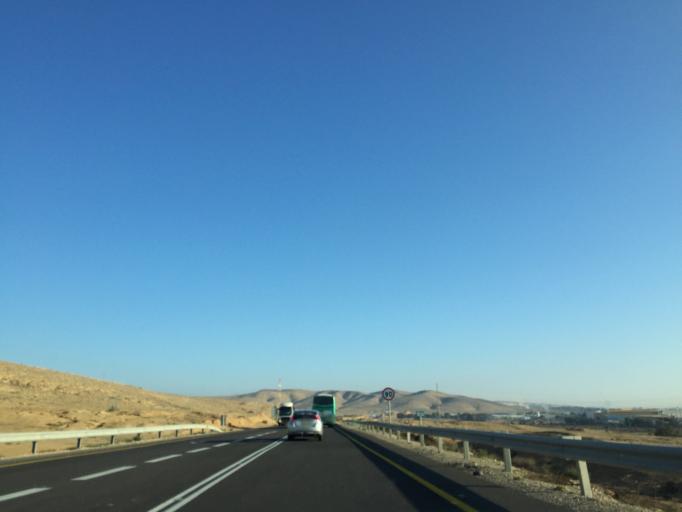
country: IL
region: Southern District
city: Dimona
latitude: 31.0565
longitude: 34.9992
